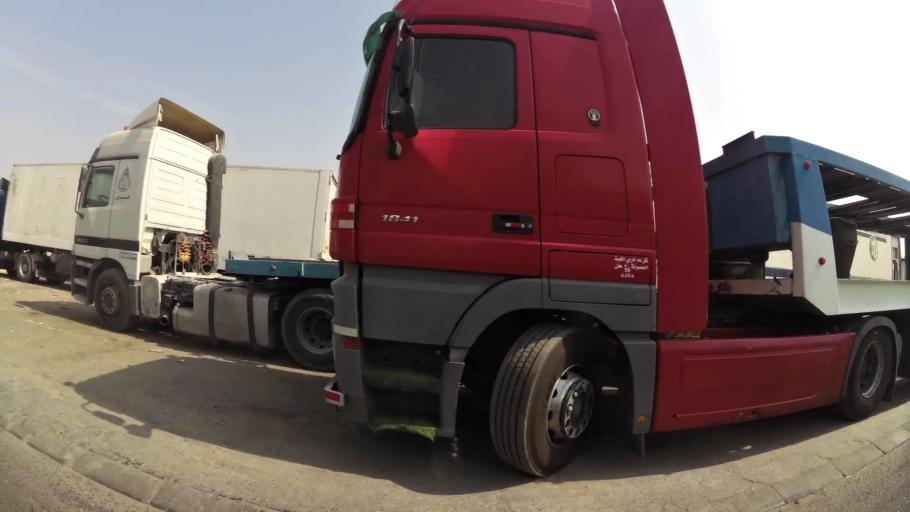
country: KW
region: Al Asimah
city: Ar Rabiyah
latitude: 29.3219
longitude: 47.9236
